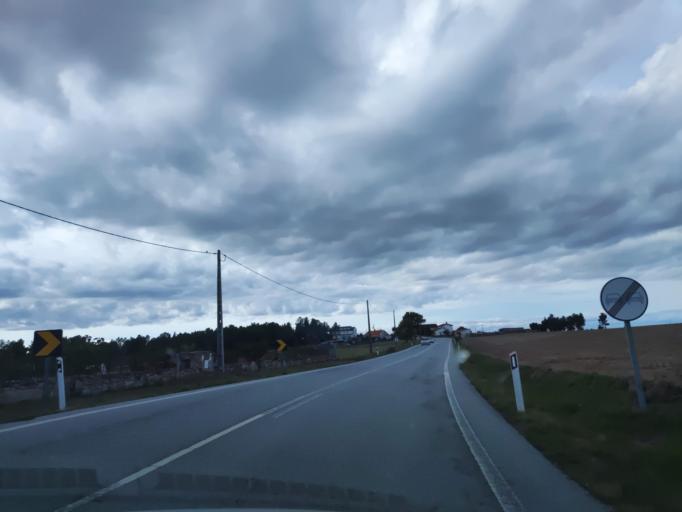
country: ES
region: Castille and Leon
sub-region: Provincia de Salamanca
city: Aldea del Obispo
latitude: 40.6723
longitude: -6.8626
